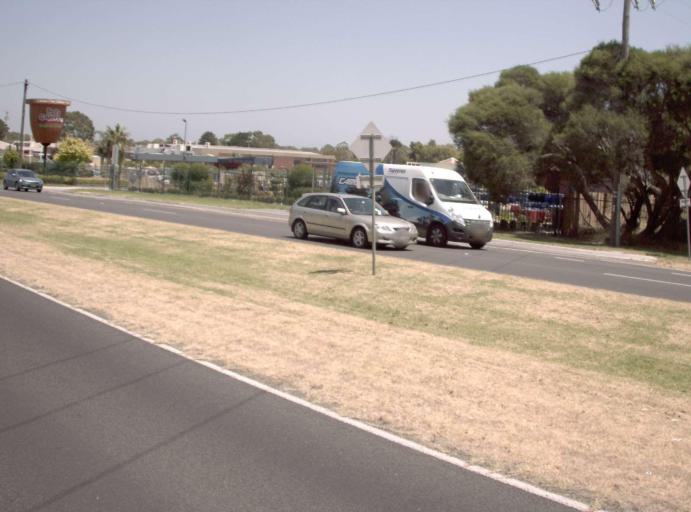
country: AU
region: Victoria
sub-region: Kingston
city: Dingley Village
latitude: -37.9991
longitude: 145.1432
